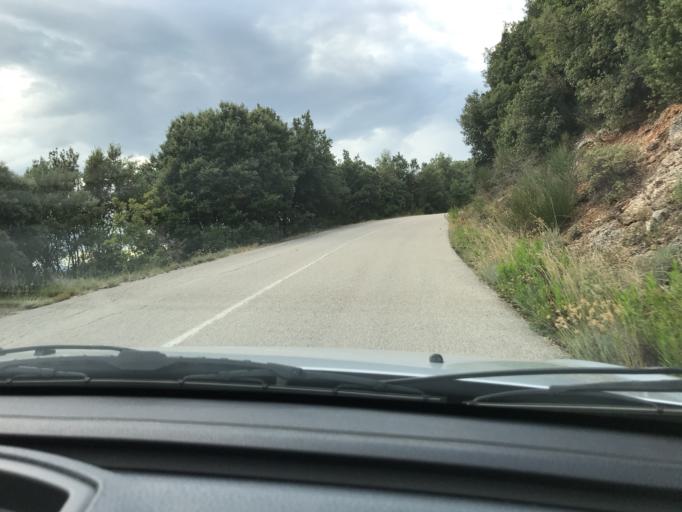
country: IT
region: Umbria
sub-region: Provincia di Terni
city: Montecchio
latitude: 42.6824
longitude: 12.3010
